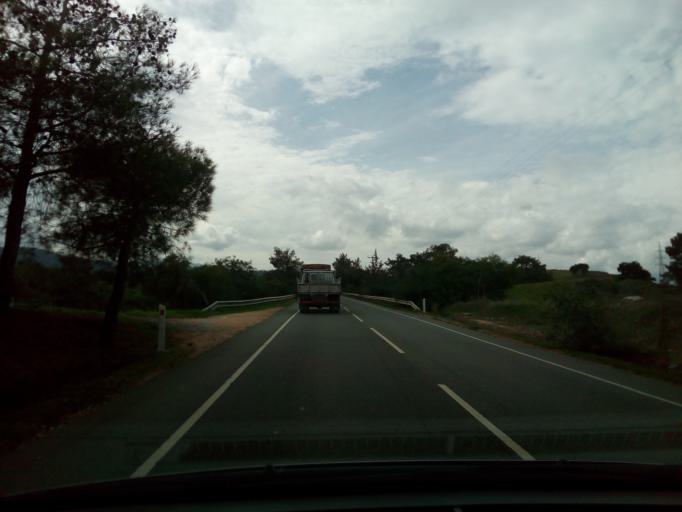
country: CY
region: Lefkosia
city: Kakopetria
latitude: 35.0763
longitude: 32.9462
